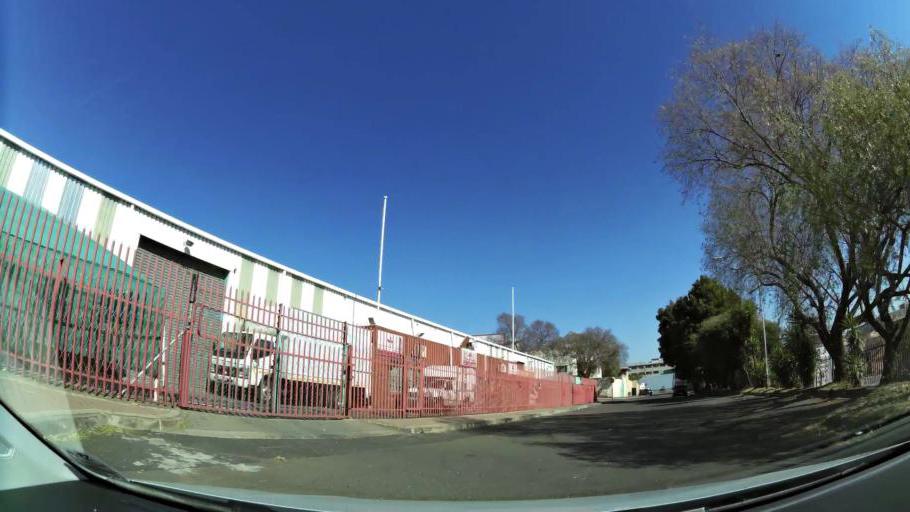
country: ZA
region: Gauteng
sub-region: City of Johannesburg Metropolitan Municipality
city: Johannesburg
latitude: -26.1975
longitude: 28.0664
